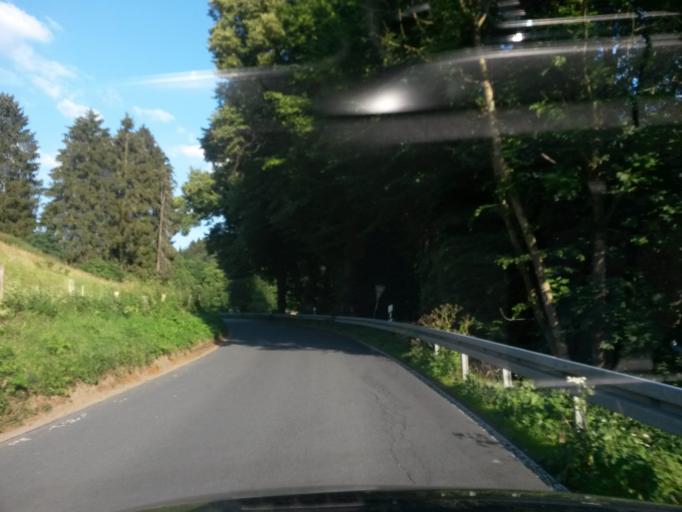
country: DE
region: North Rhine-Westphalia
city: Meinerzhagen
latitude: 51.1251
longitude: 7.6416
